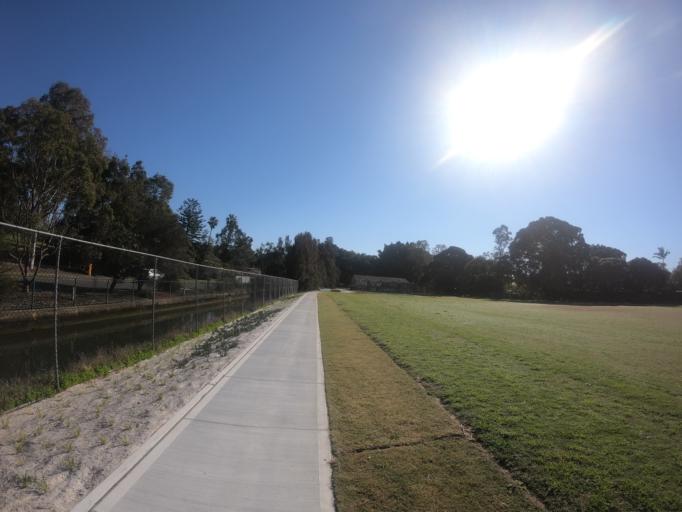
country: AU
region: New South Wales
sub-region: Hunters Hill
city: Gladesville
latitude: -33.8273
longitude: 151.1142
